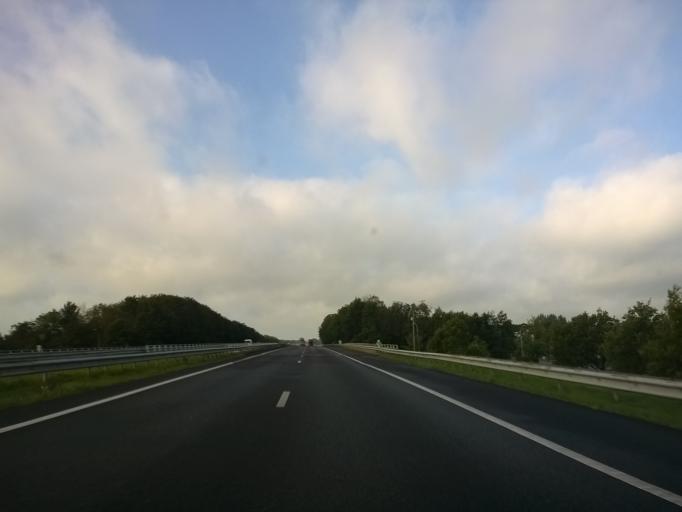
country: NL
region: Groningen
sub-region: Gemeente Grootegast
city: Grootegast
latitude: 53.1541
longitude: 6.2711
